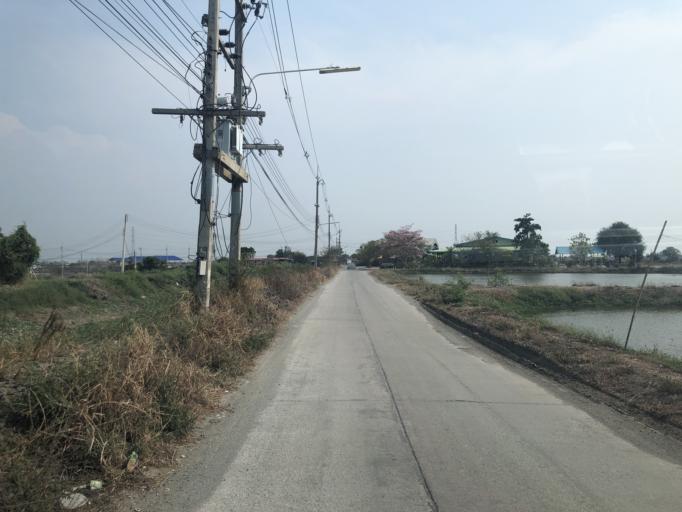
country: TH
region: Samut Prakan
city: Bang Bo
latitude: 13.5316
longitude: 100.9051
